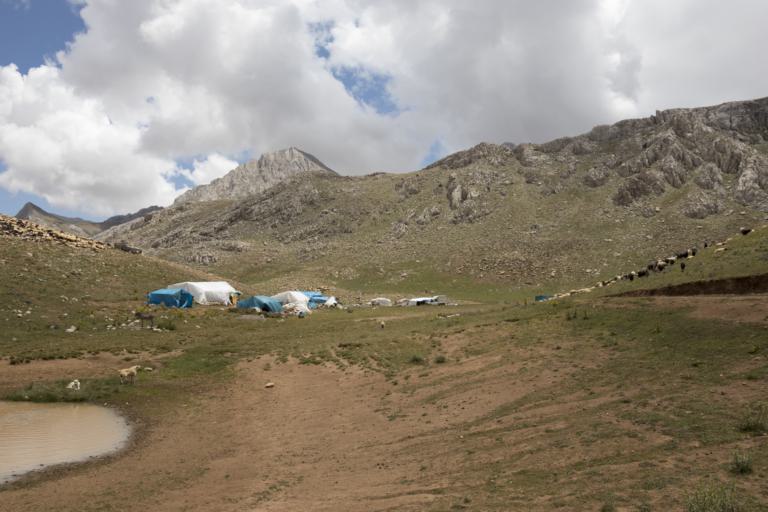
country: TR
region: Adana
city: Tufanbeyli
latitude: 38.4216
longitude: 36.1898
